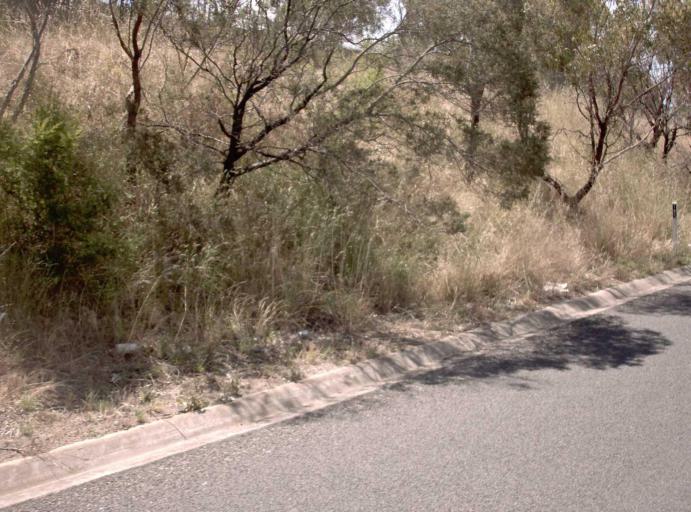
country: AU
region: Victoria
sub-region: Wellington
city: Heyfield
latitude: -38.1389
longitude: 146.7937
